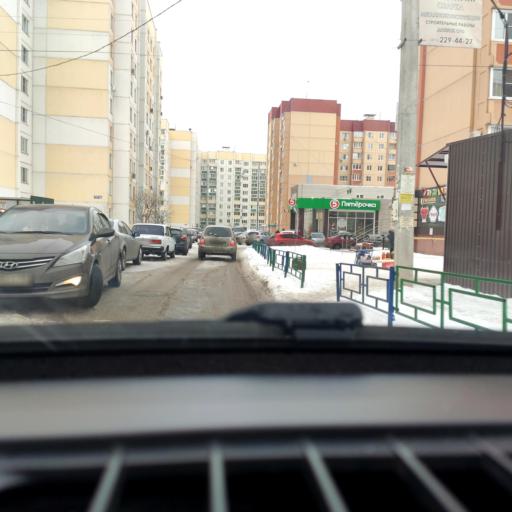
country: RU
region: Voronezj
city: Pridonskoy
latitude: 51.6204
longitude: 39.0634
